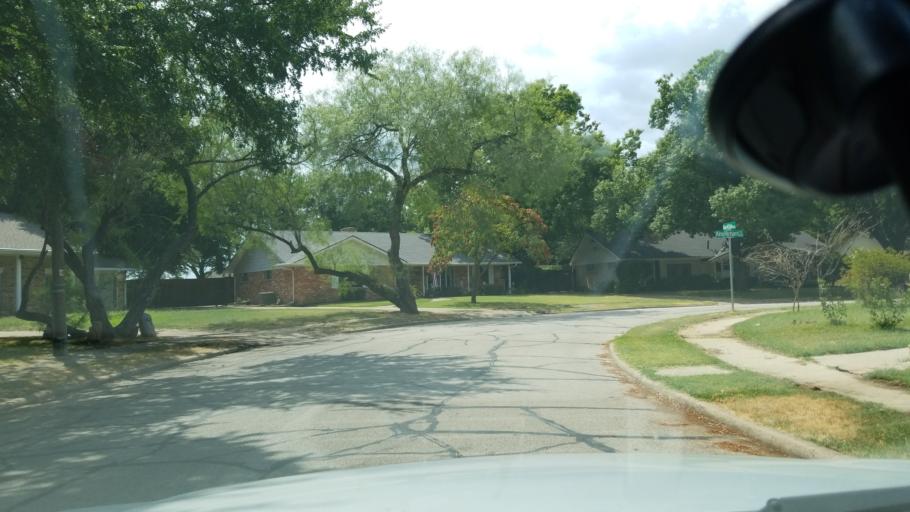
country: US
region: Texas
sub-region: Dallas County
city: Irving
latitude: 32.8169
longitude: -96.9850
